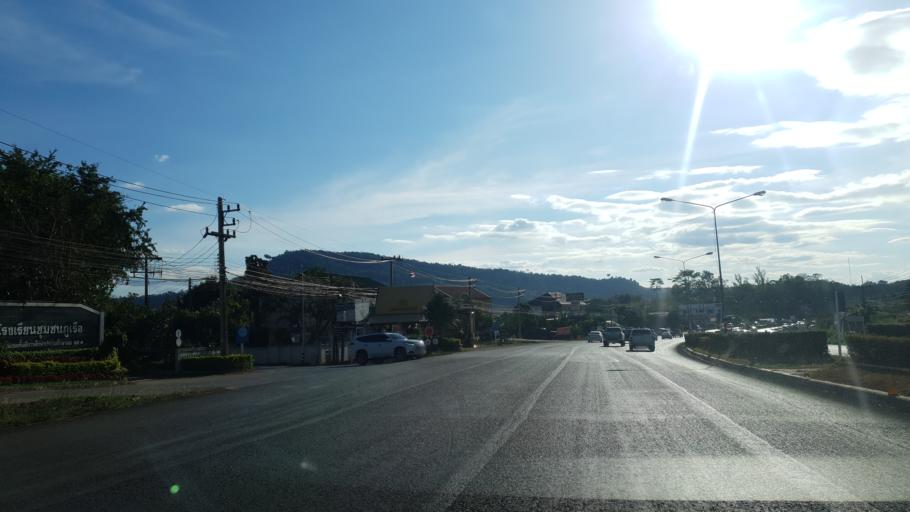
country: TH
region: Loei
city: Phu Ruea
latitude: 17.4513
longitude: 101.3605
